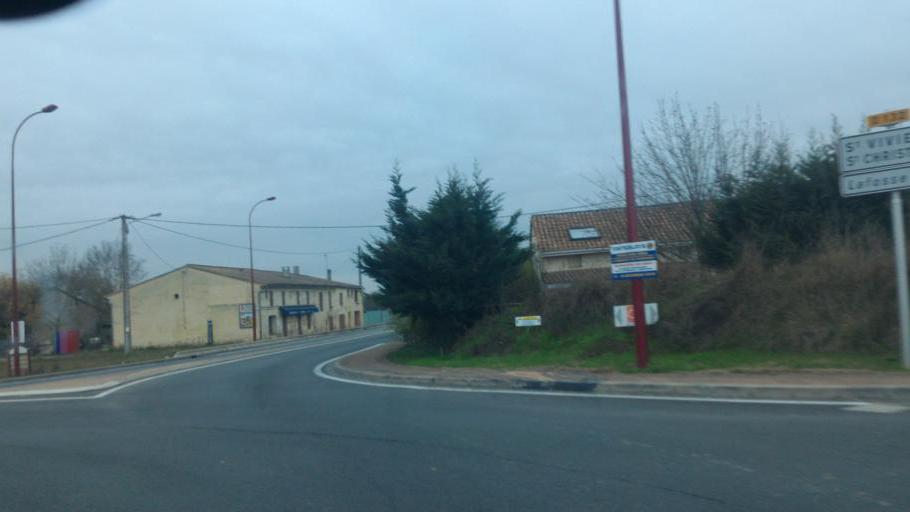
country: FR
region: Aquitaine
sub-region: Departement de la Gironde
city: Pugnac
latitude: 45.0889
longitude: -0.5178
